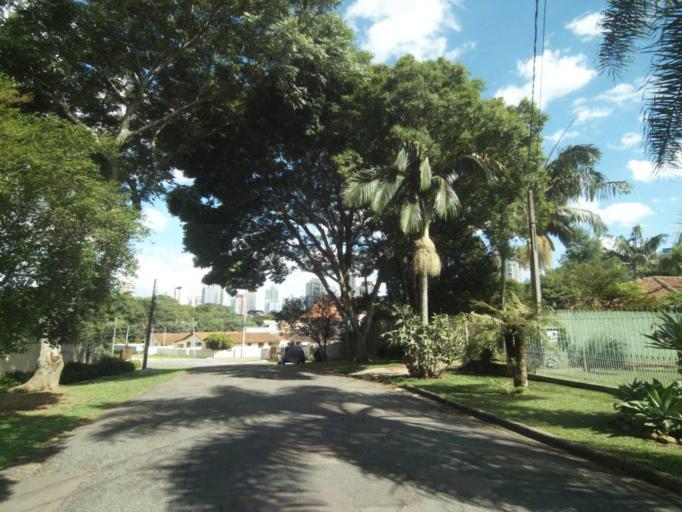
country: BR
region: Parana
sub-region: Curitiba
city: Curitiba
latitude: -25.4357
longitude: -49.3454
